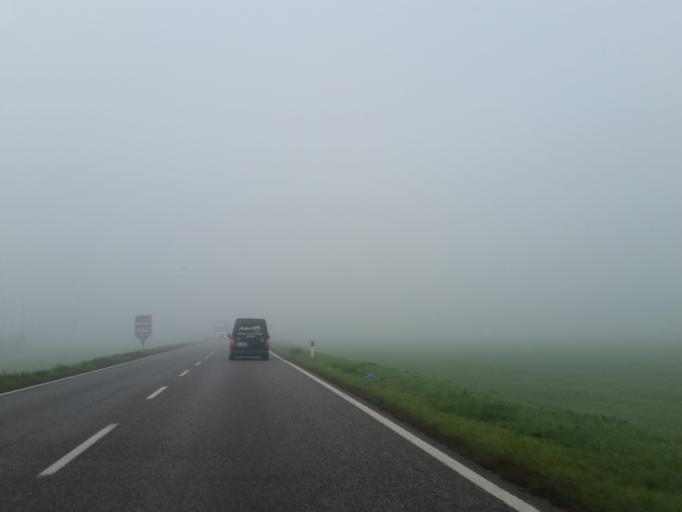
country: IT
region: Lombardy
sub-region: Provincia di Brescia
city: Orzivecchi
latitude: 45.3976
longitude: 9.9849
